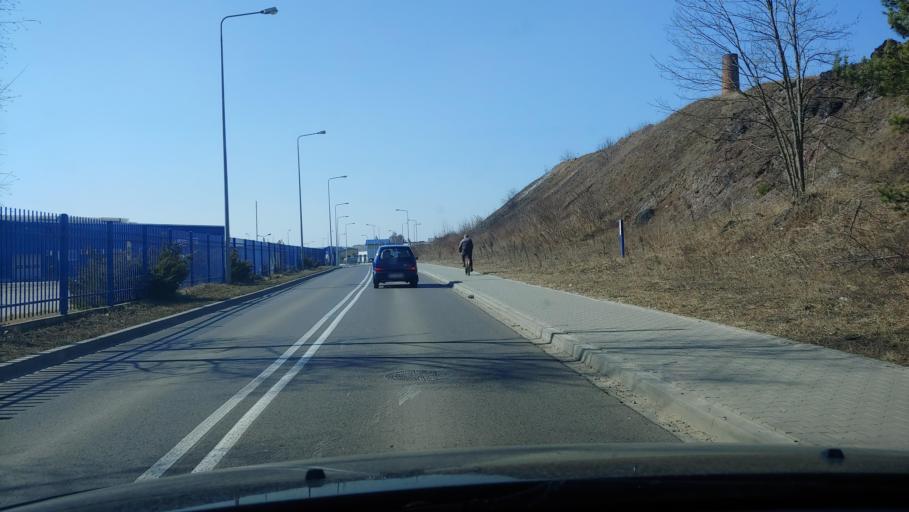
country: PL
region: Lesser Poland Voivodeship
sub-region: Powiat chrzanowski
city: Trzebinia
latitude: 50.1535
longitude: 19.4634
